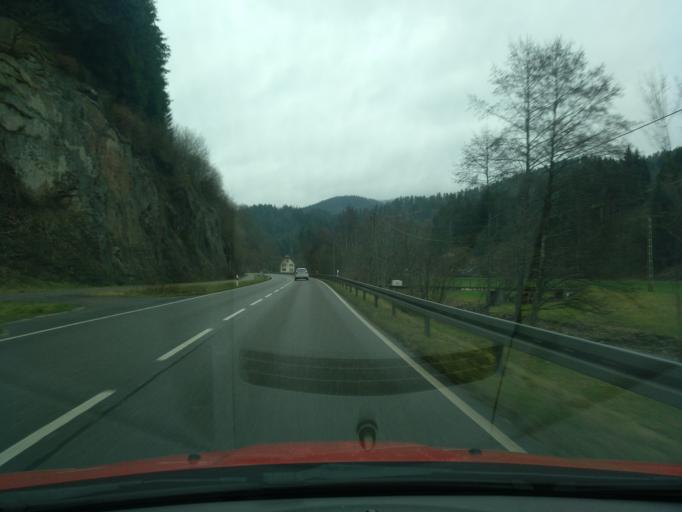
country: DE
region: Baden-Wuerttemberg
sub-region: Freiburg Region
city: Schramberg
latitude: 48.2544
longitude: 8.3724
